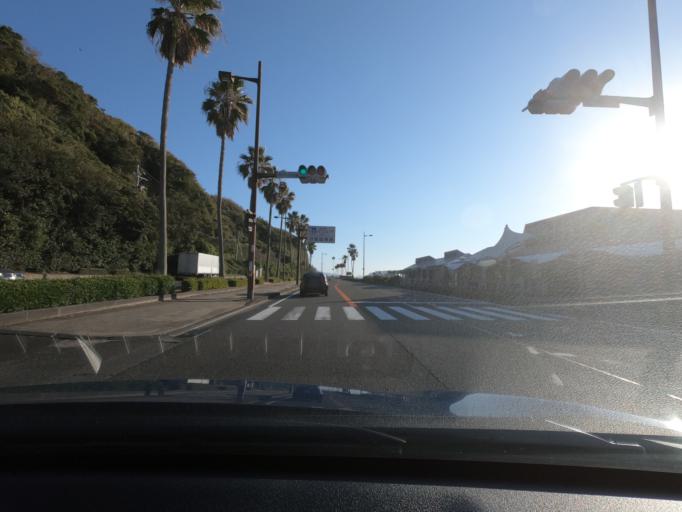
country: JP
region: Kagoshima
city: Akune
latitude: 31.9462
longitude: 130.2167
